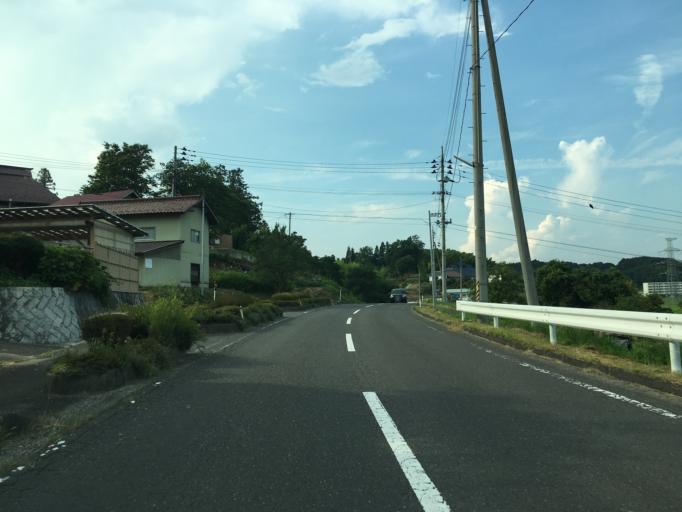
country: JP
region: Fukushima
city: Motomiya
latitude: 37.5009
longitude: 140.4330
